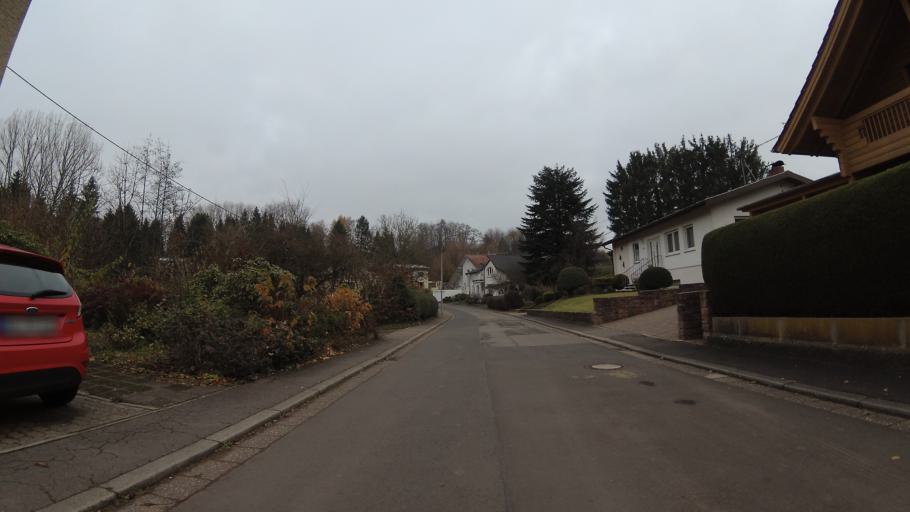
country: DE
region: Saarland
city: Schiffweiler
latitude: 49.3740
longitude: 7.1152
